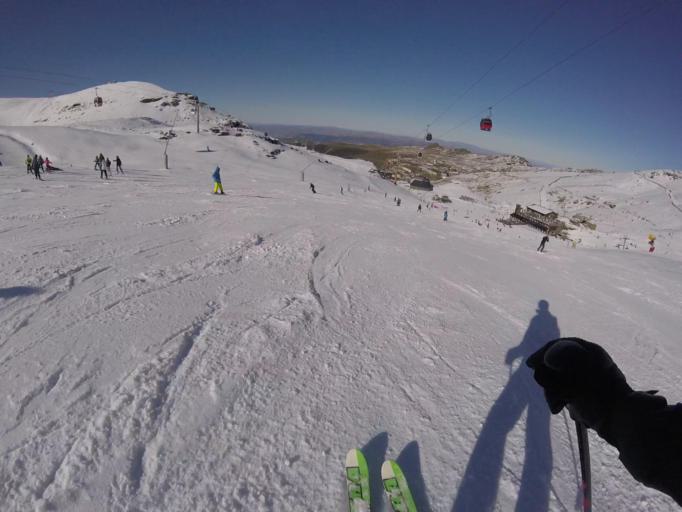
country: ES
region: Andalusia
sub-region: Provincia de Granada
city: Guejar-Sierra
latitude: 37.0745
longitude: -3.3896
